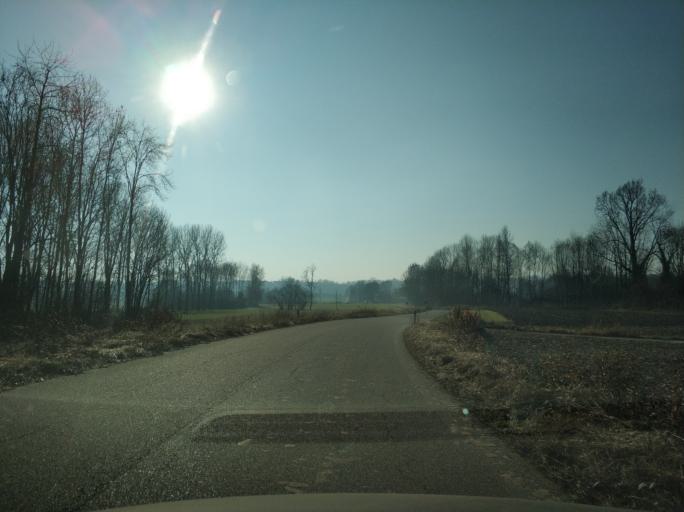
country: IT
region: Piedmont
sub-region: Provincia di Torino
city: Levone
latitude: 45.3060
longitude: 7.6157
